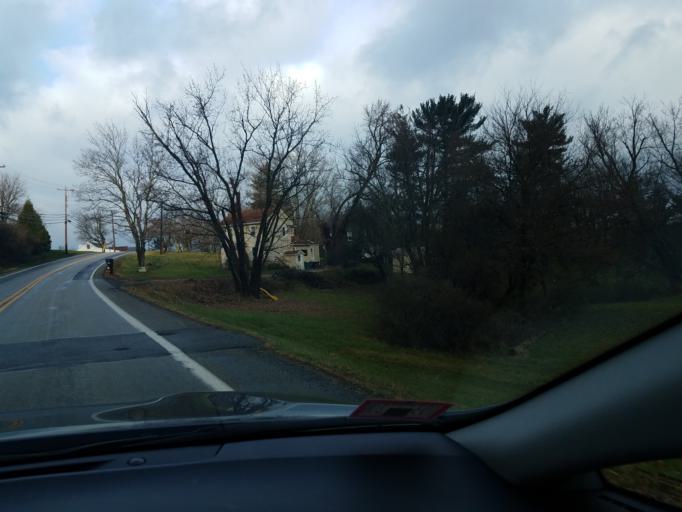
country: US
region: Pennsylvania
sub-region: Allegheny County
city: Franklin Park
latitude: 40.5817
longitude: -80.0858
